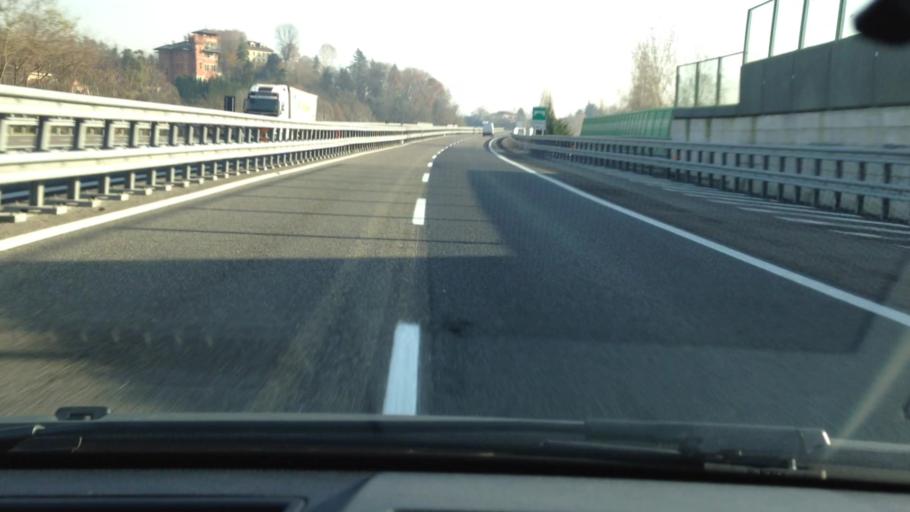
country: IT
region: Piedmont
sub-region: Provincia di Asti
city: Asti
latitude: 44.9172
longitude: 8.2057
